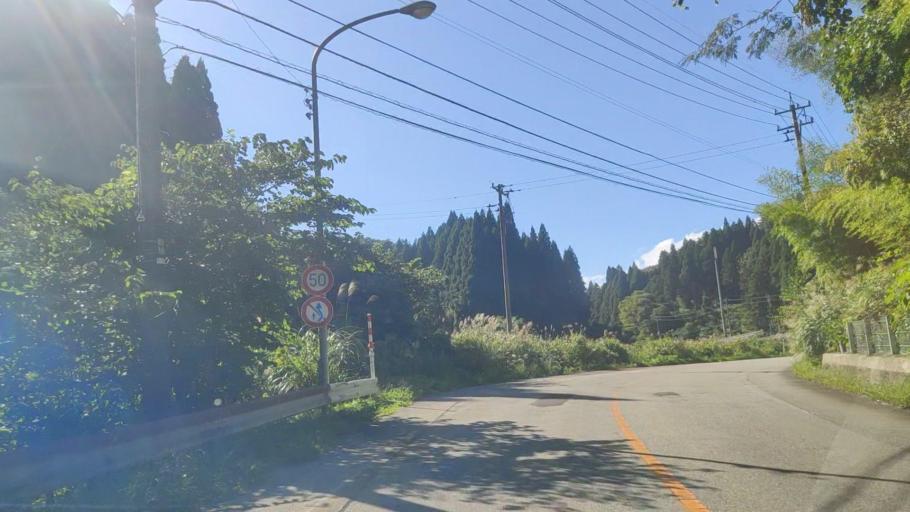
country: JP
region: Ishikawa
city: Nanao
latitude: 37.3210
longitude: 137.1849
